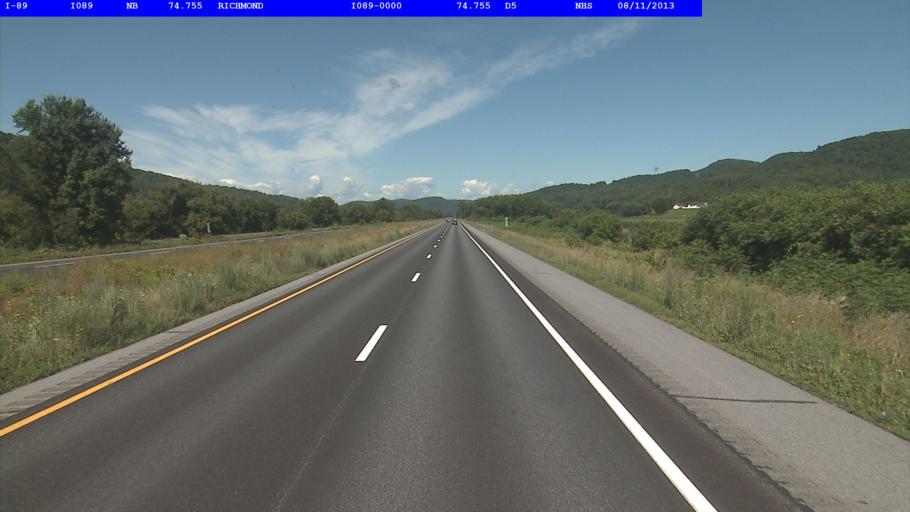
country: US
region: Vermont
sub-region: Chittenden County
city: Jericho
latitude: 44.3921
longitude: -72.9572
